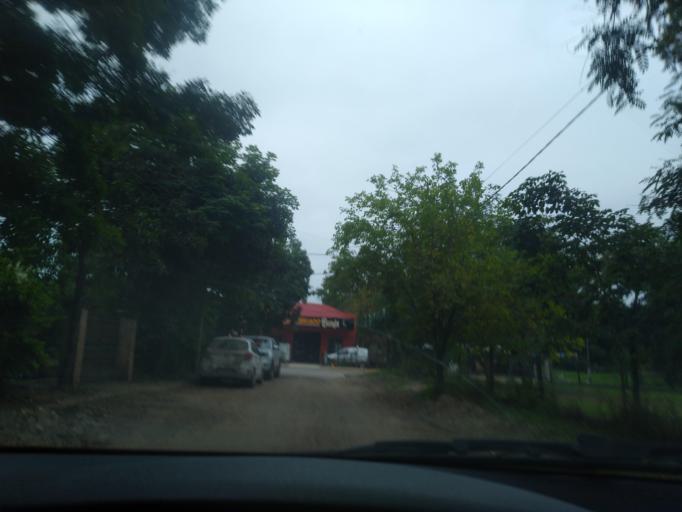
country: AR
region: Chaco
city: Colonia Benitez
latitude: -27.3291
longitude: -58.9513
